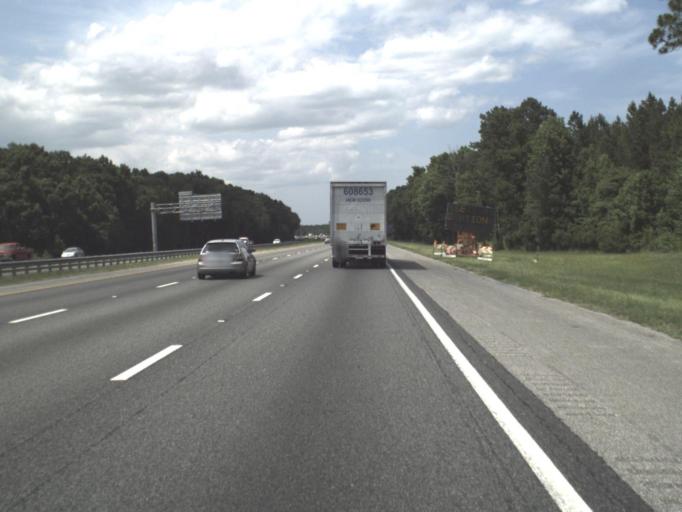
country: US
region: Florida
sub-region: Saint Johns County
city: Palm Valley
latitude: 30.0818
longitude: -81.4980
